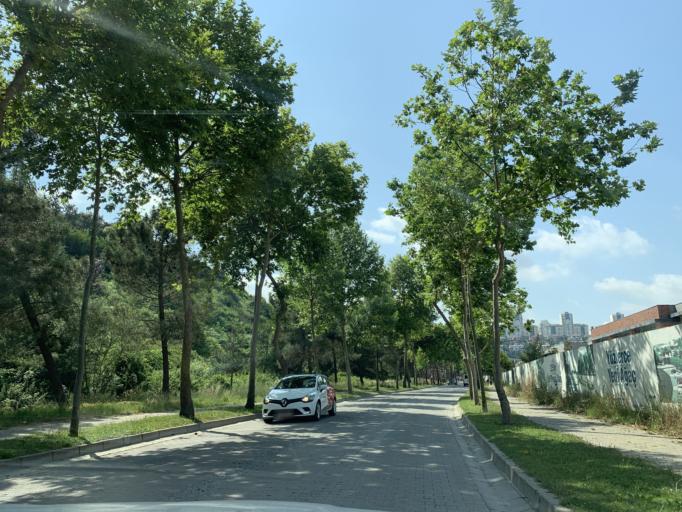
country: TR
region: Istanbul
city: Esenyurt
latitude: 41.0649
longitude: 28.6948
